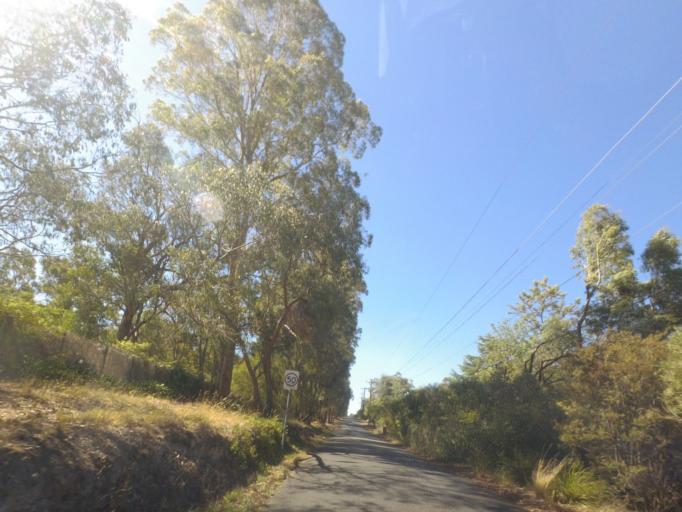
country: AU
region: Victoria
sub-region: Yarra Ranges
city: Chirnside Park
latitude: -37.7232
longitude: 145.2850
